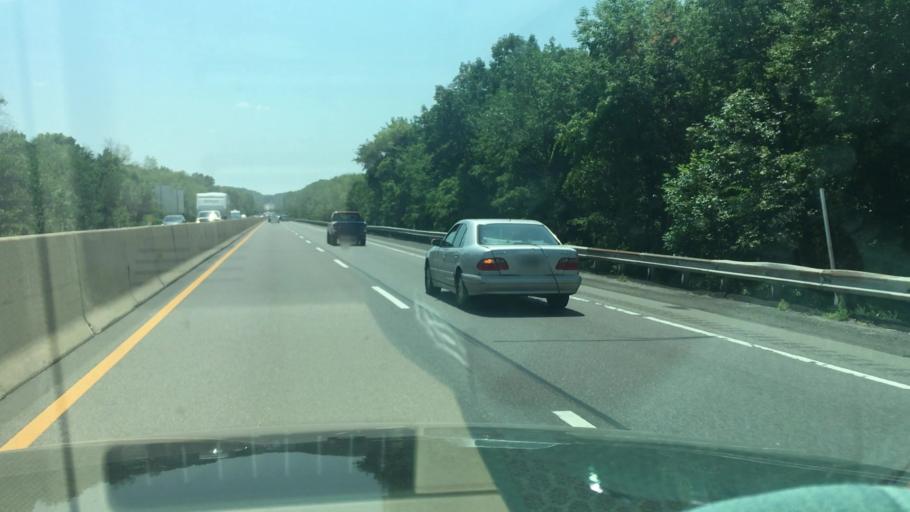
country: US
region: Pennsylvania
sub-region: Bucks County
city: Spinnerstown
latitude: 40.4091
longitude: -75.4134
